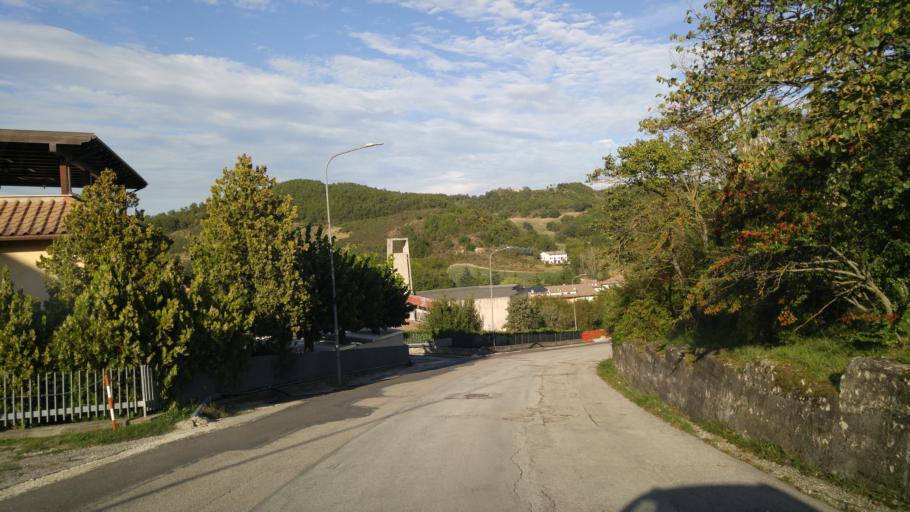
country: IT
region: The Marches
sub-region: Provincia di Pesaro e Urbino
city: Cagli
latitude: 43.5443
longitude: 12.6572
